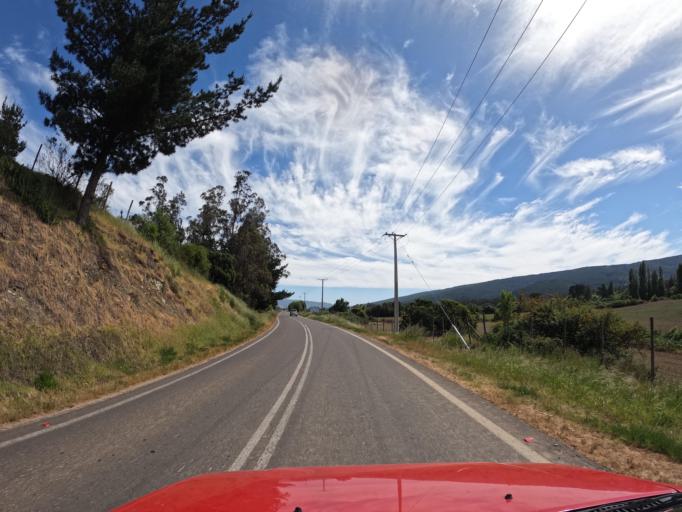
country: CL
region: Maule
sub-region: Provincia de Talca
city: Constitucion
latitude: -34.9948
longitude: -72.0195
